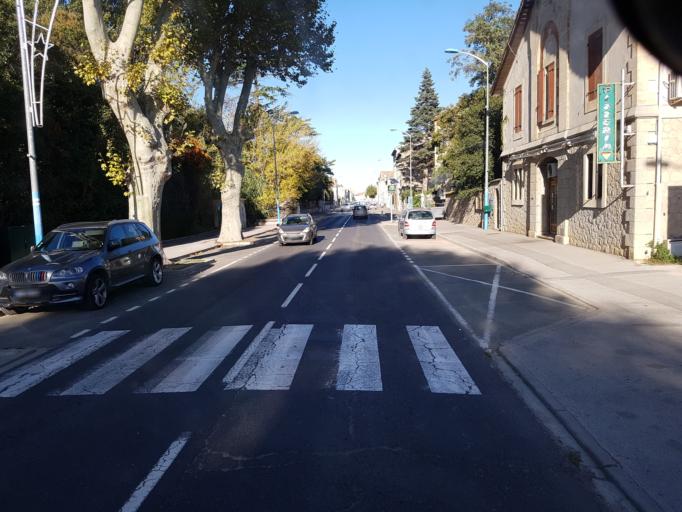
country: FR
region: Languedoc-Roussillon
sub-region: Departement de l'Aude
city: Coursan
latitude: 43.2301
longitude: 3.0525
